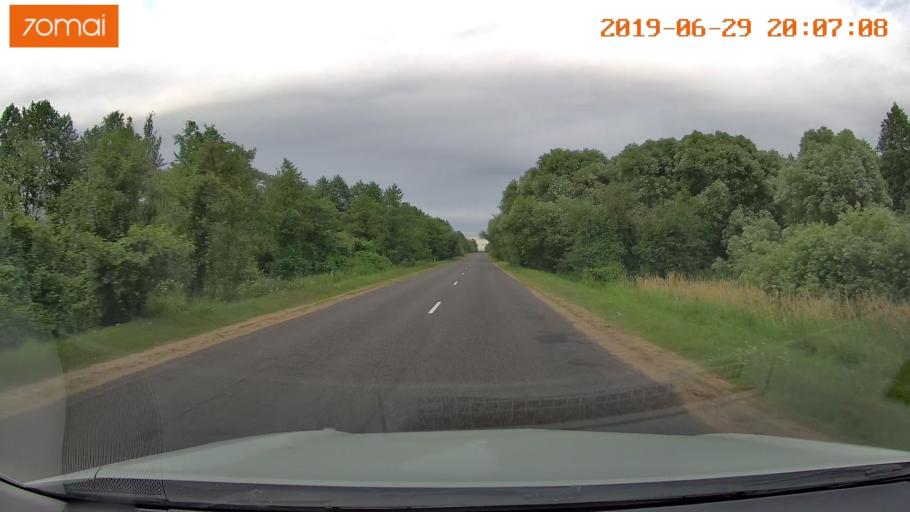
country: BY
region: Brest
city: Lahishyn
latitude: 52.3404
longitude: 26.0286
